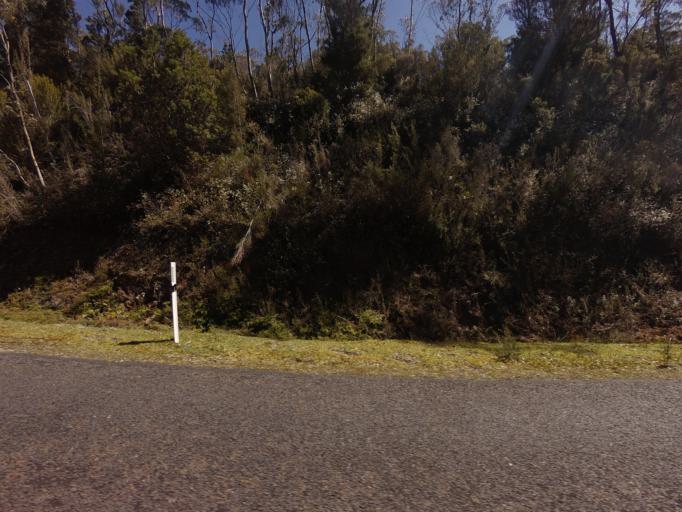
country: AU
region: Tasmania
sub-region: Derwent Valley
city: New Norfolk
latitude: -42.7220
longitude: 146.4448
